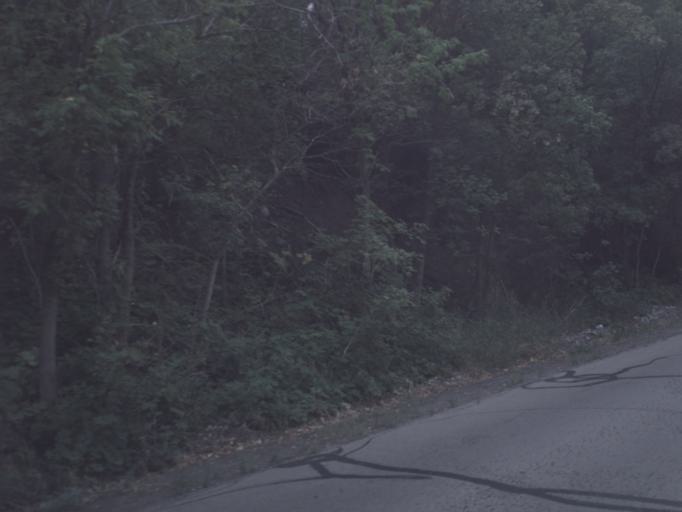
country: US
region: Utah
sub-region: Utah County
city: Cedar Hills
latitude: 40.4448
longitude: -111.6984
